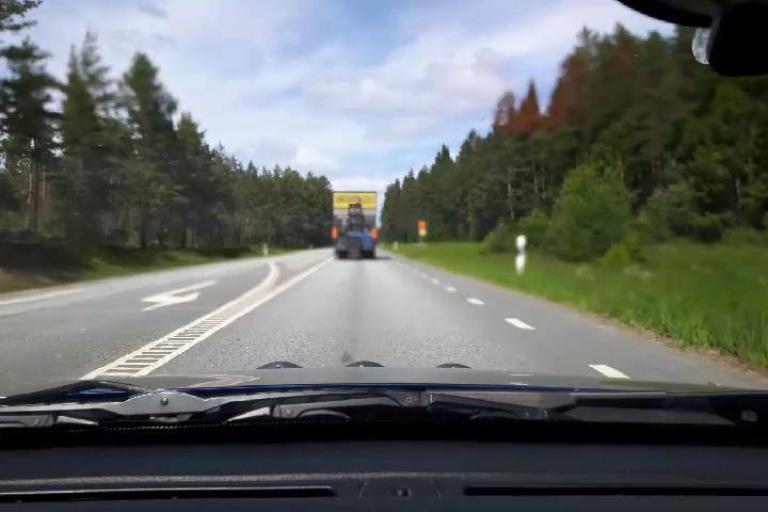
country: SE
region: Uppsala
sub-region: Tierps Kommun
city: Tierp
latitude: 60.1843
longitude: 17.4787
